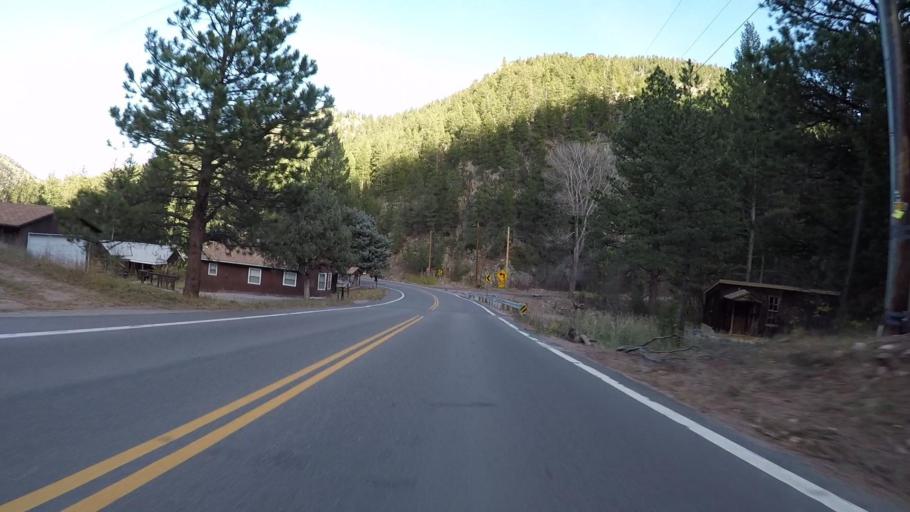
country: US
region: Colorado
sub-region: Boulder County
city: Boulder
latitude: 40.0815
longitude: -105.3673
